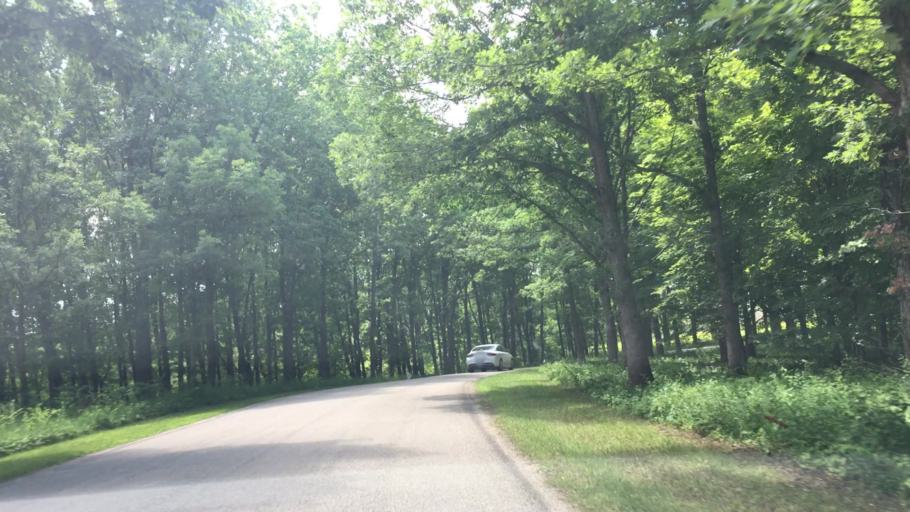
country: US
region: Iowa
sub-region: Johnson County
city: Tiffin
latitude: 41.7266
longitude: -91.7235
